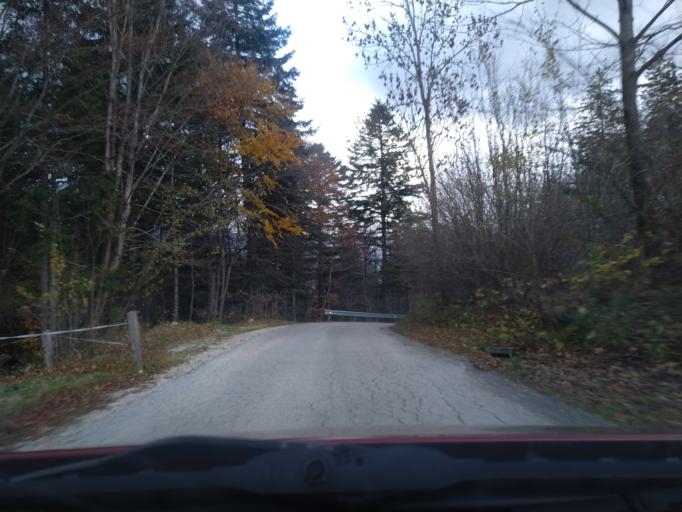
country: SI
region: Kamnik
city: Mekinje
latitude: 46.2838
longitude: 14.6887
